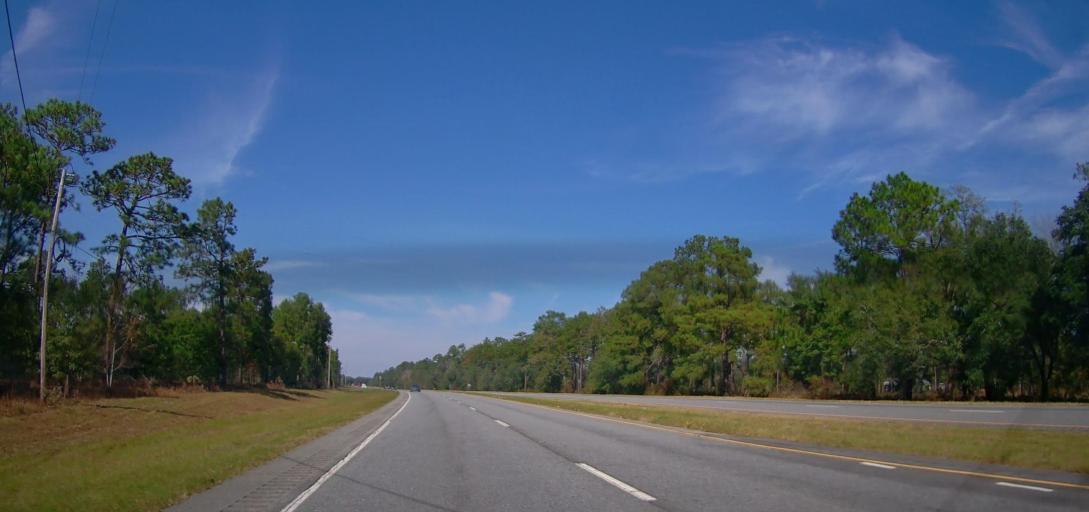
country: US
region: Georgia
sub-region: Lee County
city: Leesburg
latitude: 31.7341
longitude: -83.9862
